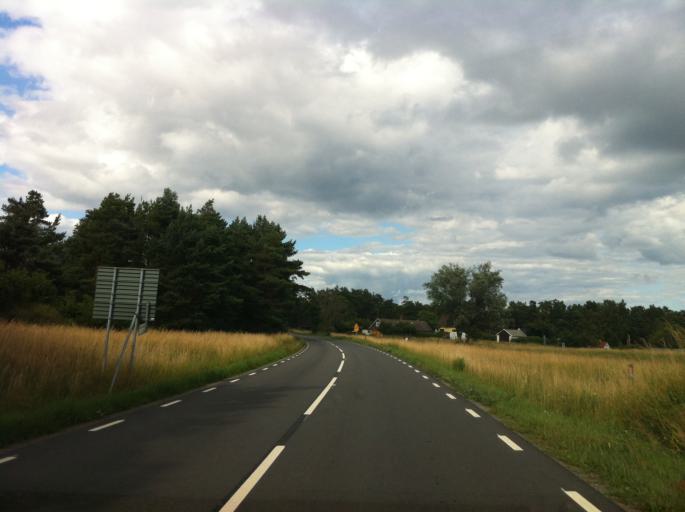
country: SE
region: Skane
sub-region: Simrishamns Kommun
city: Simrishamn
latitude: 55.4033
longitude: 14.1851
